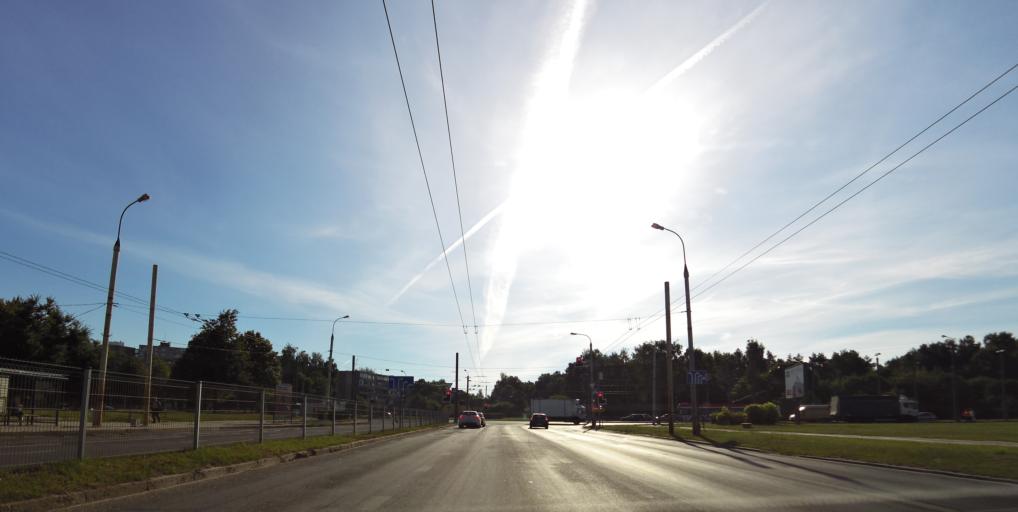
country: LT
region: Vilnius County
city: Justiniskes
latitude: 54.7034
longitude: 25.2232
